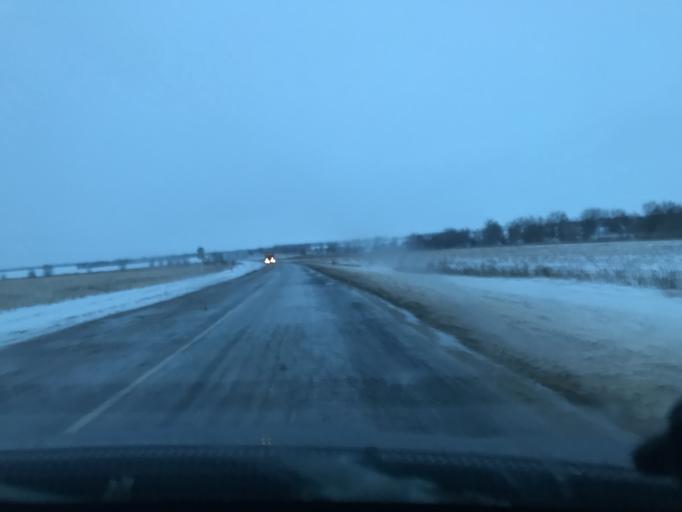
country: RU
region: Rostov
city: Letnik
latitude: 46.0044
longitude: 41.2138
